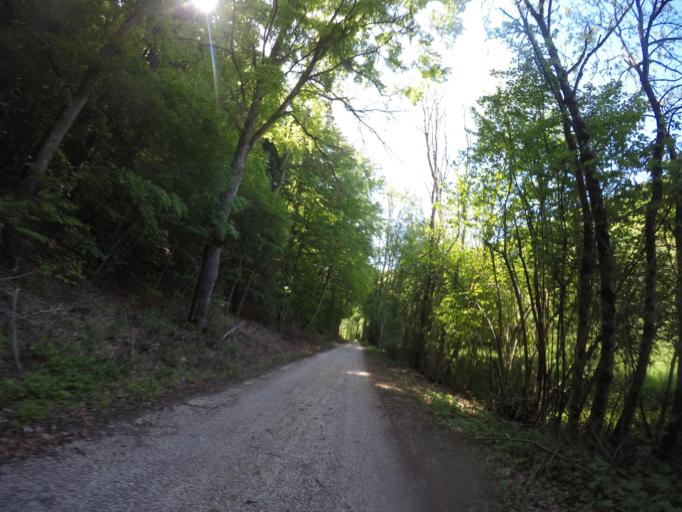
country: DE
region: Baden-Wuerttemberg
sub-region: Tuebingen Region
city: Blaubeuren
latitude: 48.3990
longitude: 9.7580
